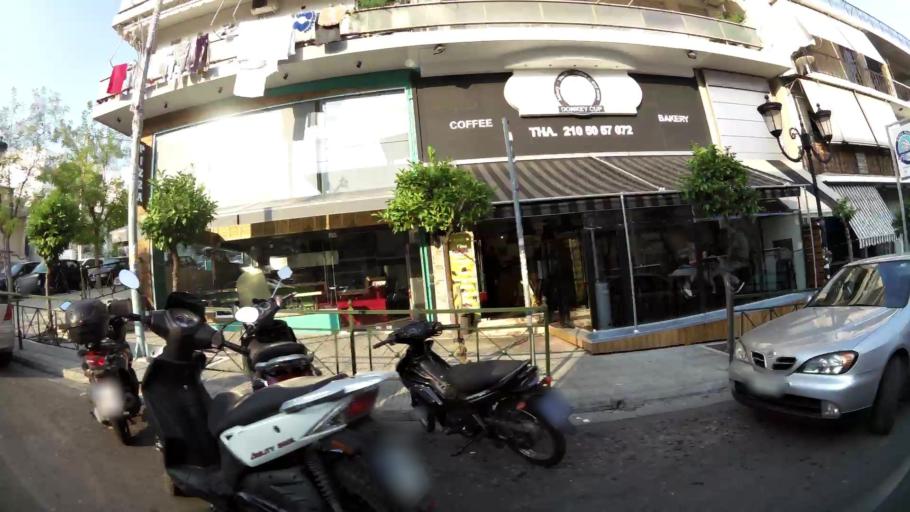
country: GR
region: Attica
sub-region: Nomarchia Athinas
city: Petroupolis
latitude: 38.0446
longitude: 23.6794
